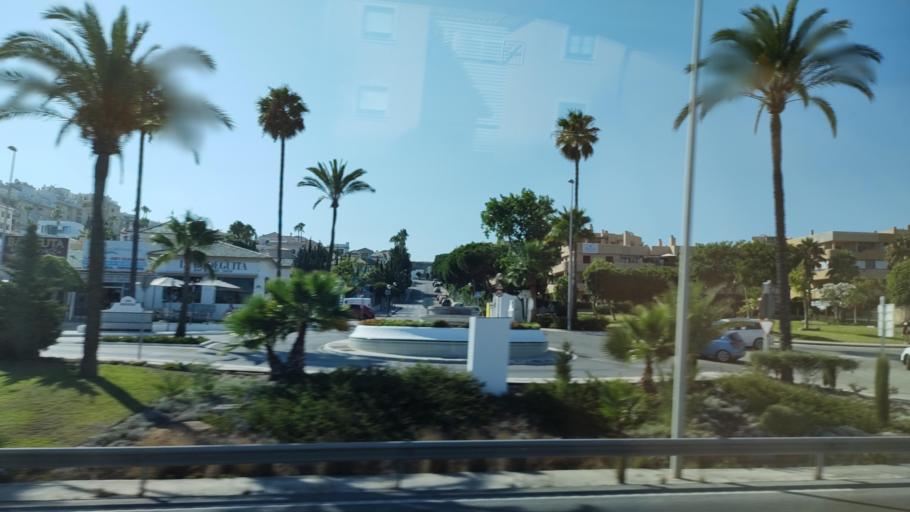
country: ES
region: Andalusia
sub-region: Provincia de Malaga
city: Fuengirola
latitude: 36.4994
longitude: -4.6871
